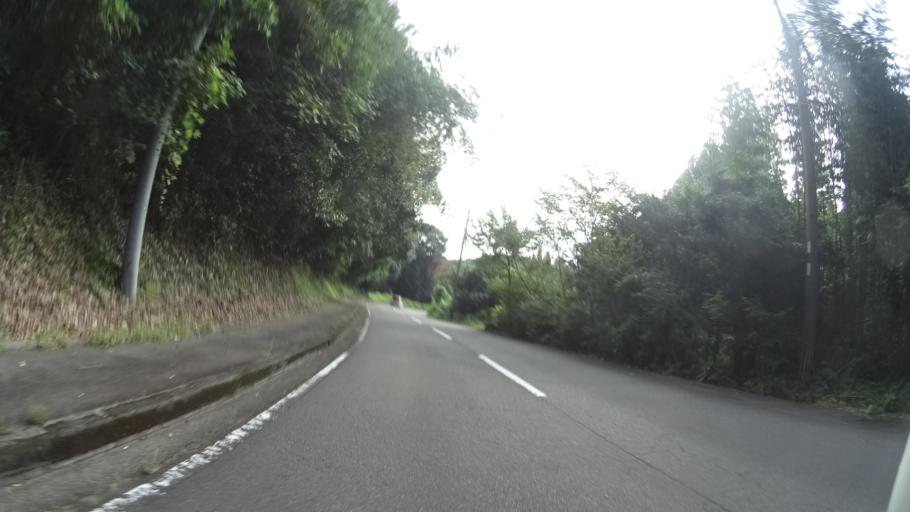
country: JP
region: Kagoshima
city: Okuchi-shinohara
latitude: 32.0168
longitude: 130.6511
